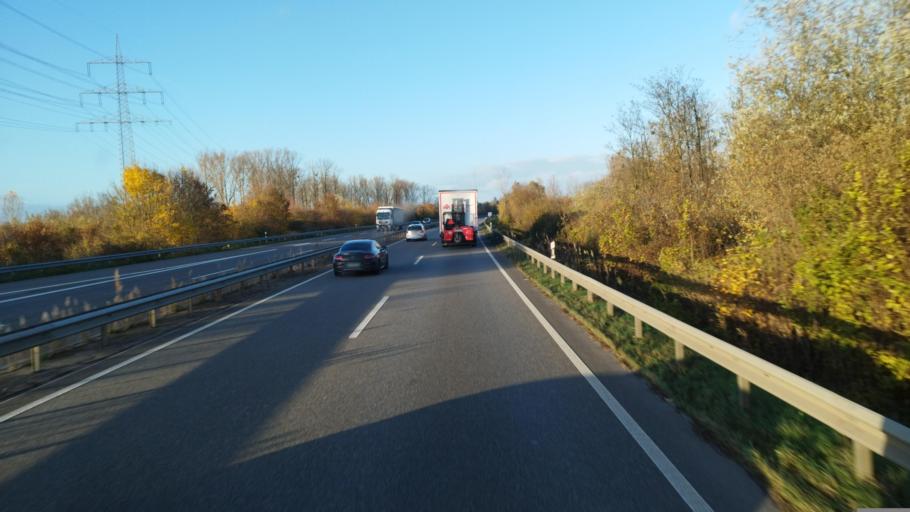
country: DE
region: Rheinland-Pfalz
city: Worth am Rhein
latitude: 49.0547
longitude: 8.2736
